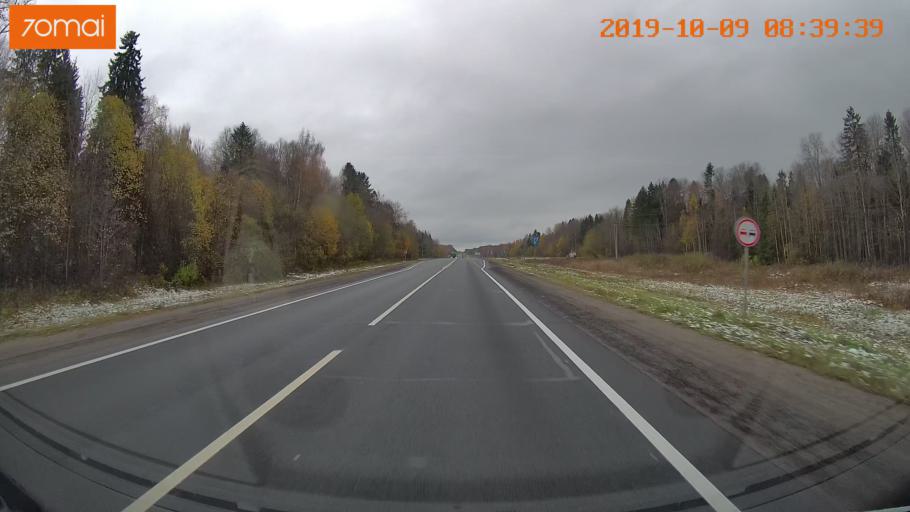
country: RU
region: Vologda
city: Gryazovets
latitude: 58.9747
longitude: 40.1505
